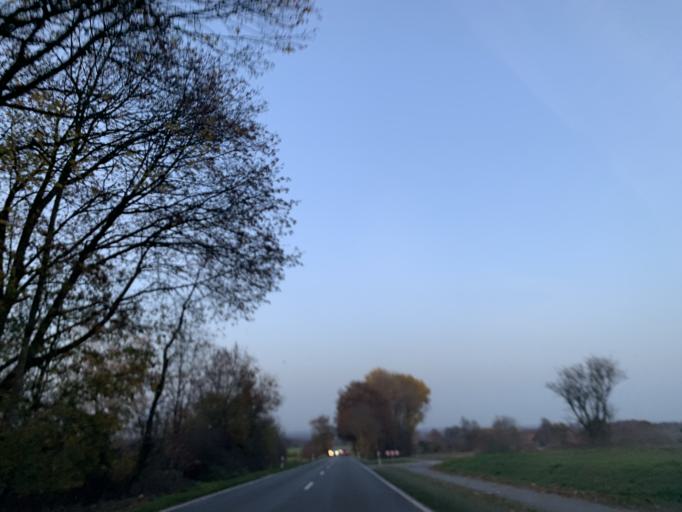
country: DE
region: North Rhine-Westphalia
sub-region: Regierungsbezirk Munster
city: Nottuln
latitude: 51.9765
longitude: 7.3504
